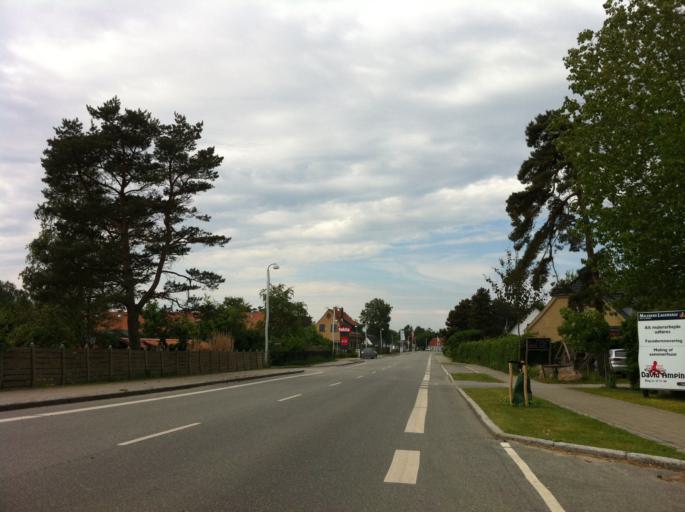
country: DK
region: Capital Region
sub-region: Gribskov Kommune
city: Graested
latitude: 56.1174
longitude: 12.2410
